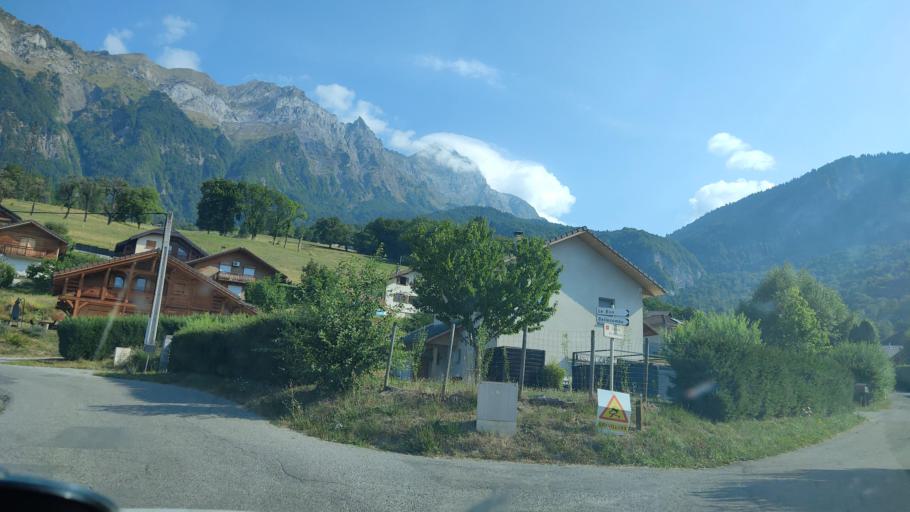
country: FR
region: Rhone-Alpes
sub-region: Departement de la Savoie
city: Ugine
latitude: 45.7615
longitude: 6.4088
